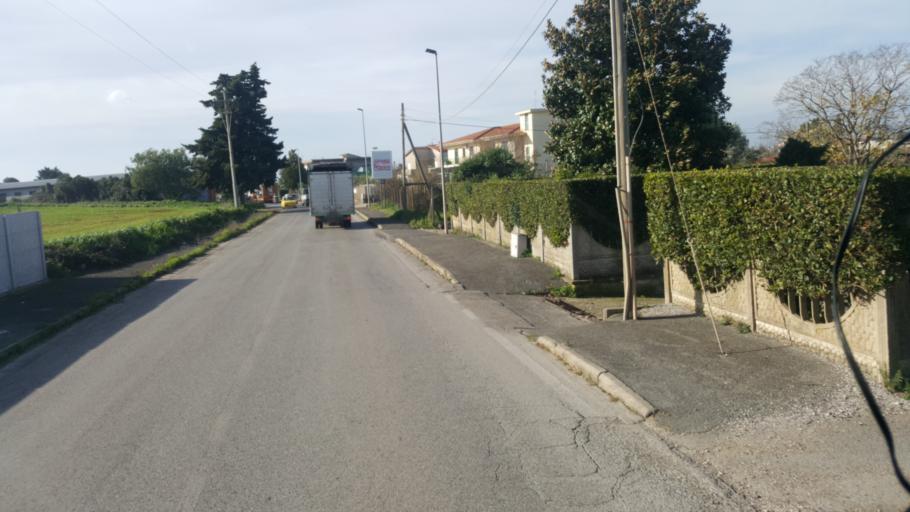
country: IT
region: Latium
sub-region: Provincia di Latina
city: Casalazzara
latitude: 41.6279
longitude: 12.5935
